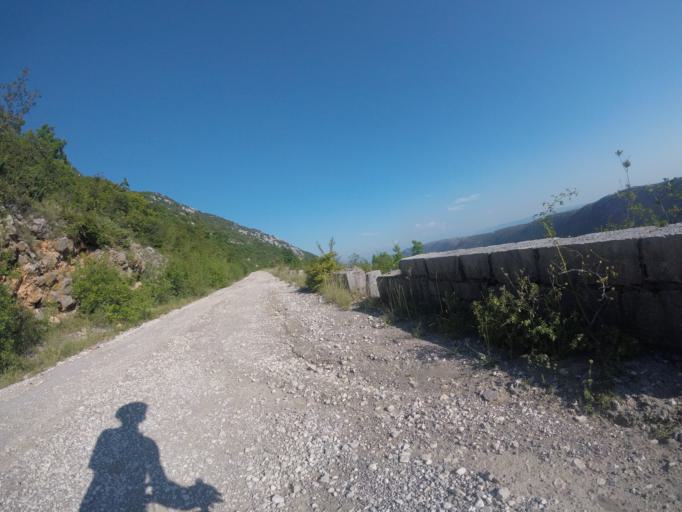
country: HR
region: Primorsko-Goranska
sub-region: Grad Crikvenica
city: Jadranovo
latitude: 45.2567
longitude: 14.6259
